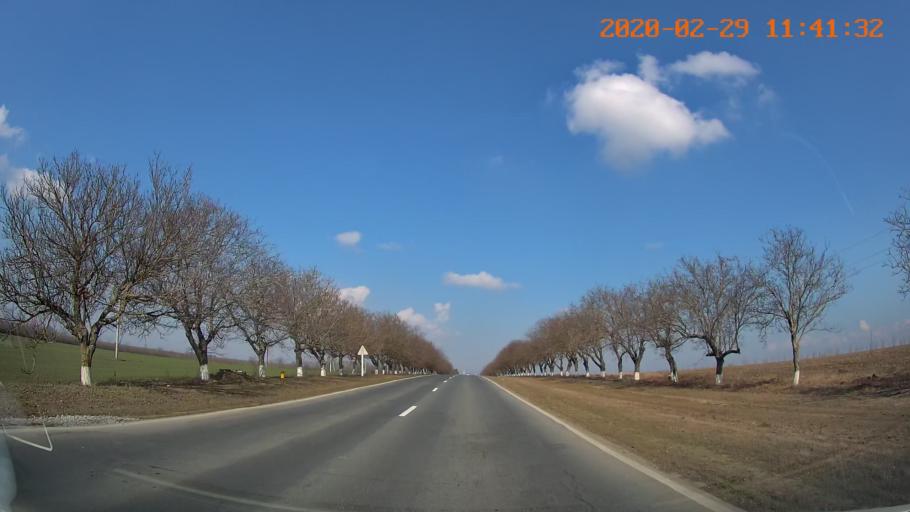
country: MD
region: Rezina
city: Saharna
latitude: 47.6726
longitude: 29.0162
